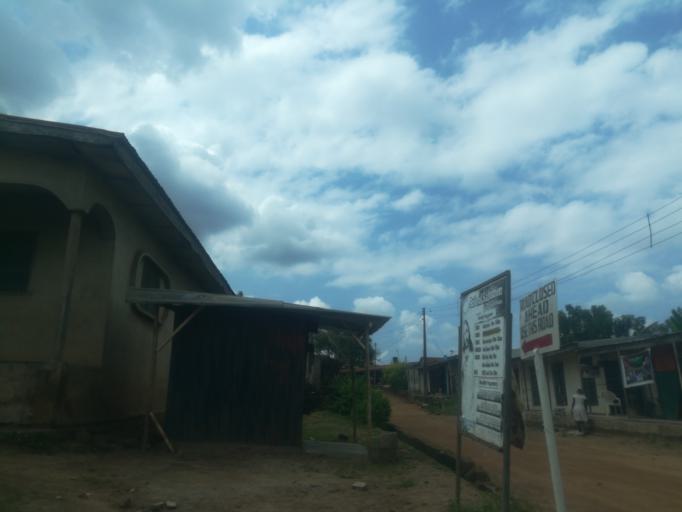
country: NG
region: Oyo
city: Egbeda
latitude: 7.4186
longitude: 4.0007
